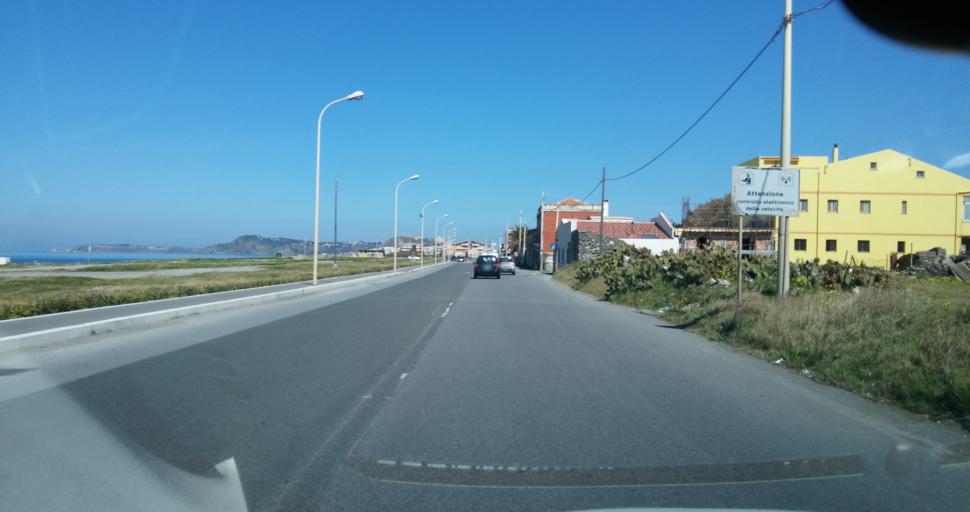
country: IT
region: Sicily
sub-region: Messina
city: Milazzo
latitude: 38.2007
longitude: 15.2243
